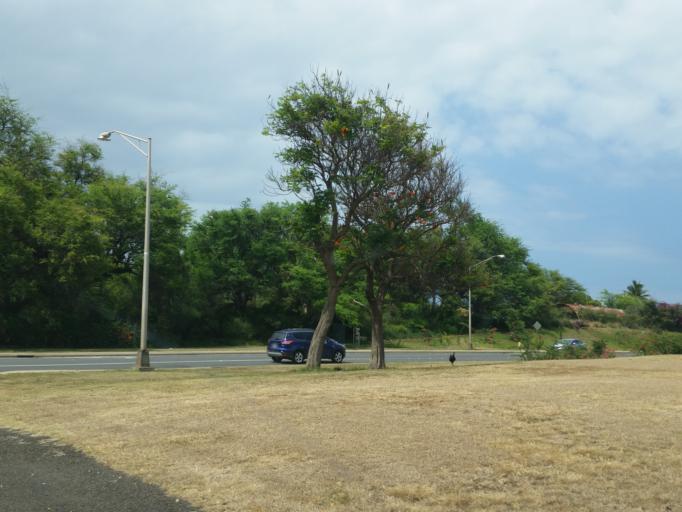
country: US
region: Hawaii
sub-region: Maui County
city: Kahului
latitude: 20.8896
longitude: -156.4478
